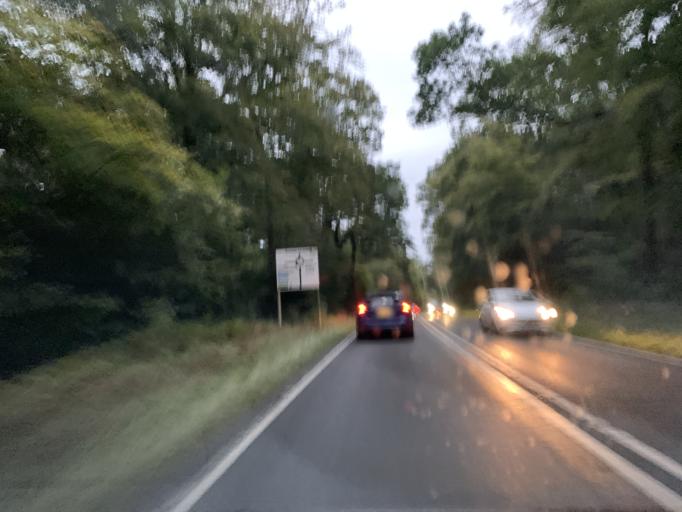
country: GB
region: England
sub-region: Hampshire
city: Cadnam
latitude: 50.9183
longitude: -1.5825
